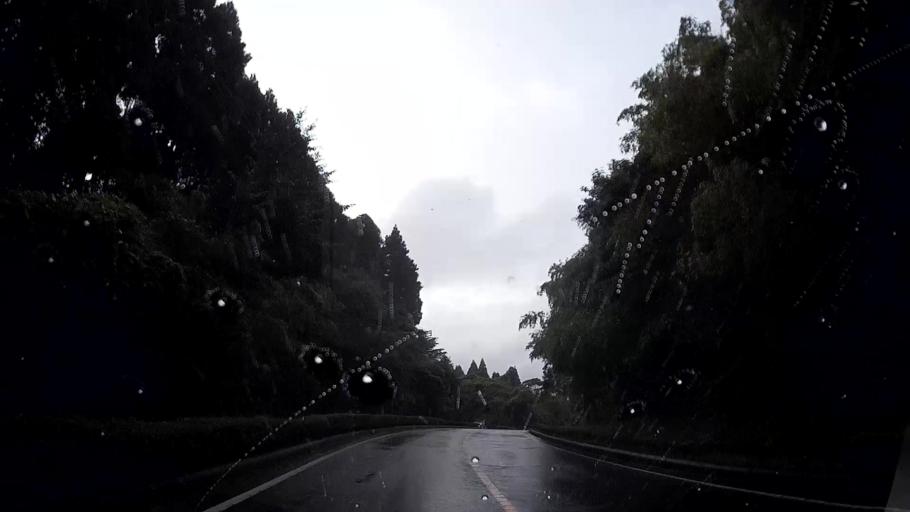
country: JP
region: Kumamoto
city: Aso
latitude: 32.8574
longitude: 131.0079
